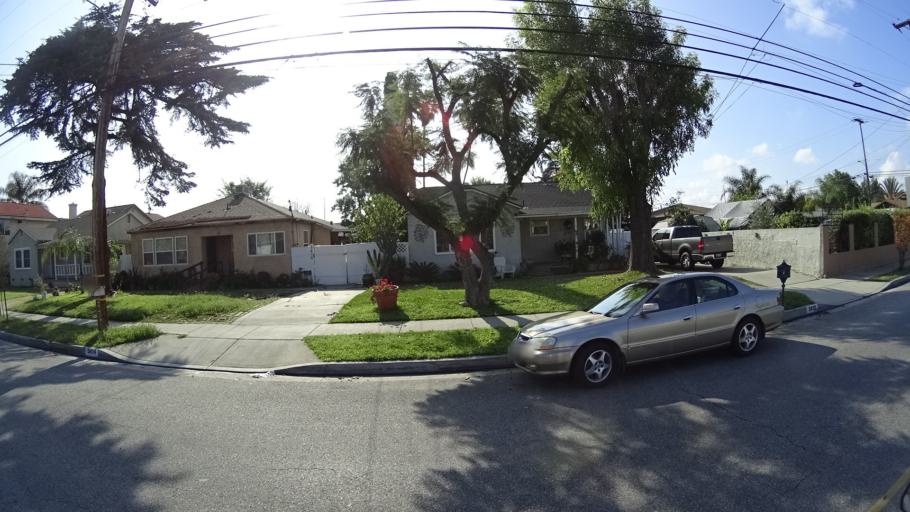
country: US
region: California
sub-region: Los Angeles County
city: Baldwin Park
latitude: 34.0756
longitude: -117.9647
